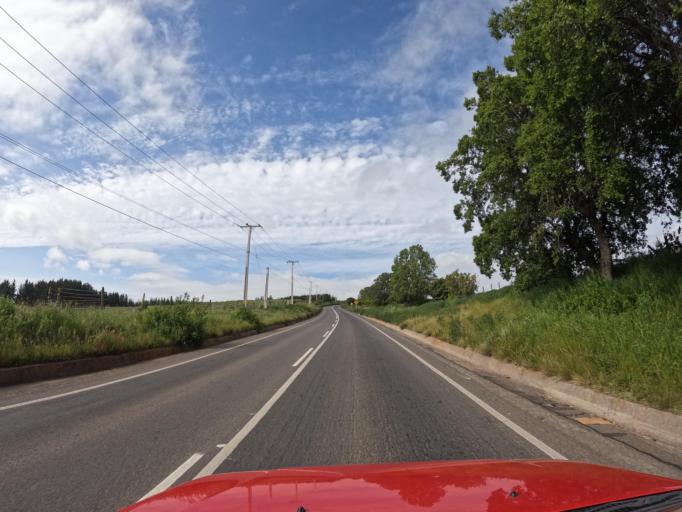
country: CL
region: O'Higgins
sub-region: Provincia de Colchagua
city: Santa Cruz
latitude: -34.3638
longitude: -71.9511
